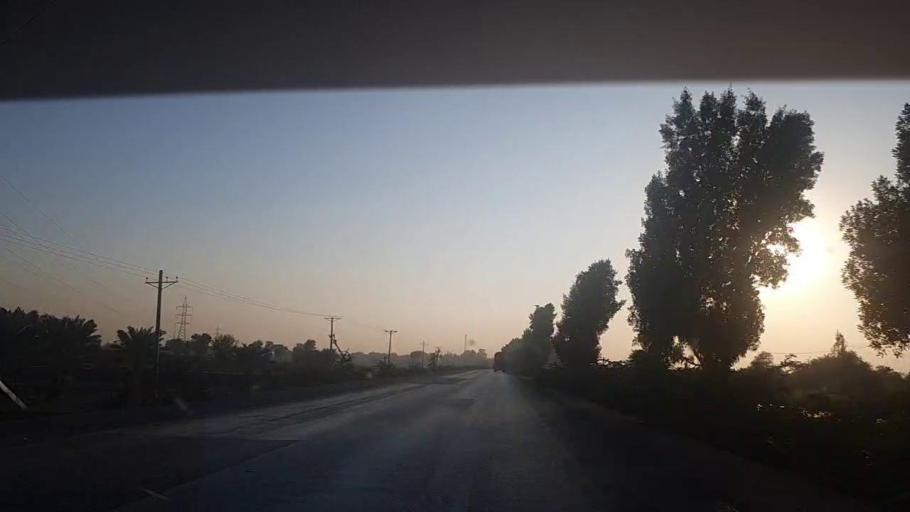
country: PK
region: Sindh
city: Hingorja
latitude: 27.1762
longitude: 68.3957
